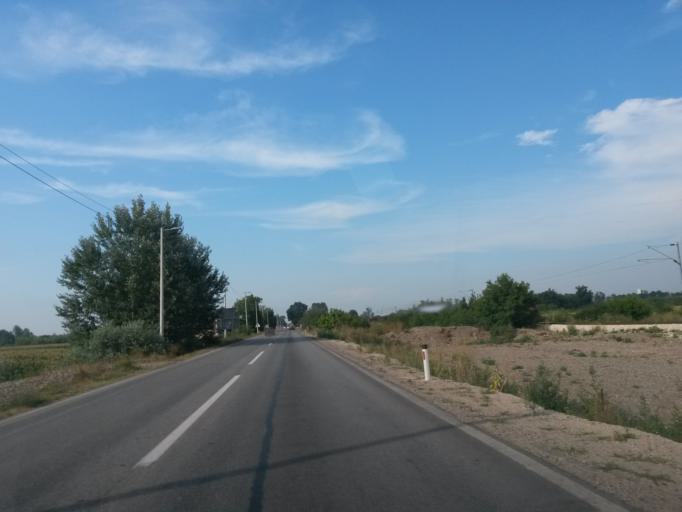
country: BA
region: Republika Srpska
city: Bosanski Samac
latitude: 45.0441
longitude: 18.4550
